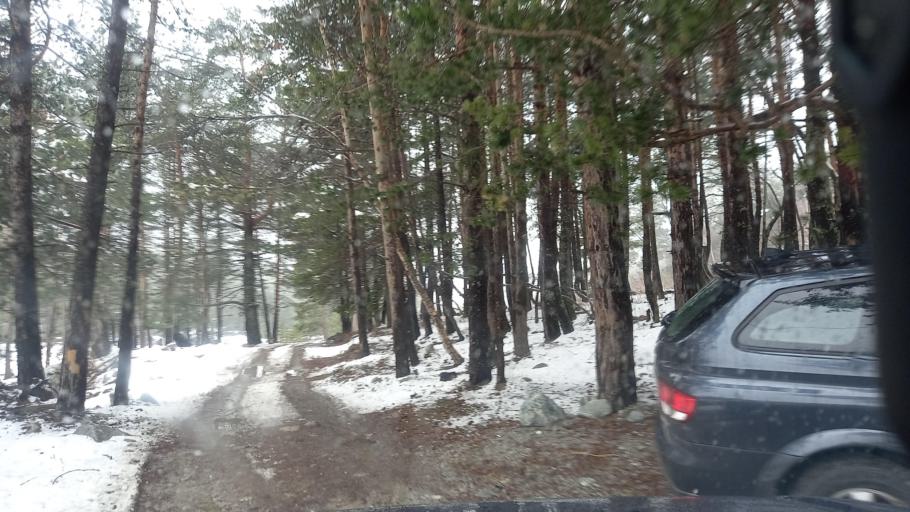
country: RU
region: Kabardino-Balkariya
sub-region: El'brusskiy Rayon
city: El'brus
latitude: 43.2186
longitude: 42.6949
